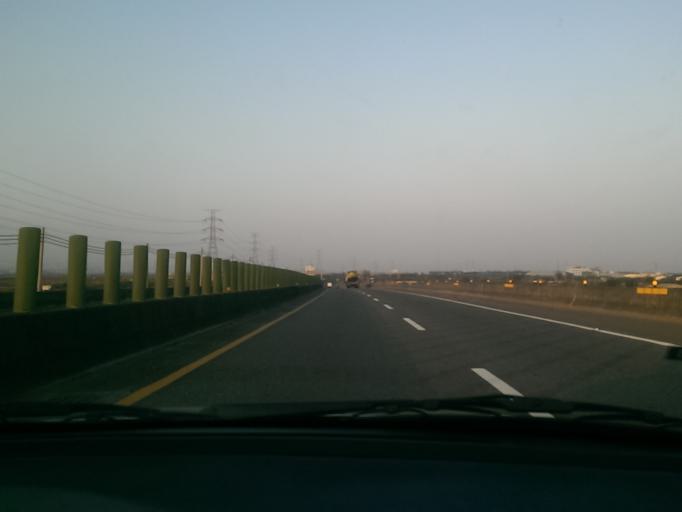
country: TW
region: Taiwan
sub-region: Changhua
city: Chang-hua
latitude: 24.1750
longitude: 120.4786
